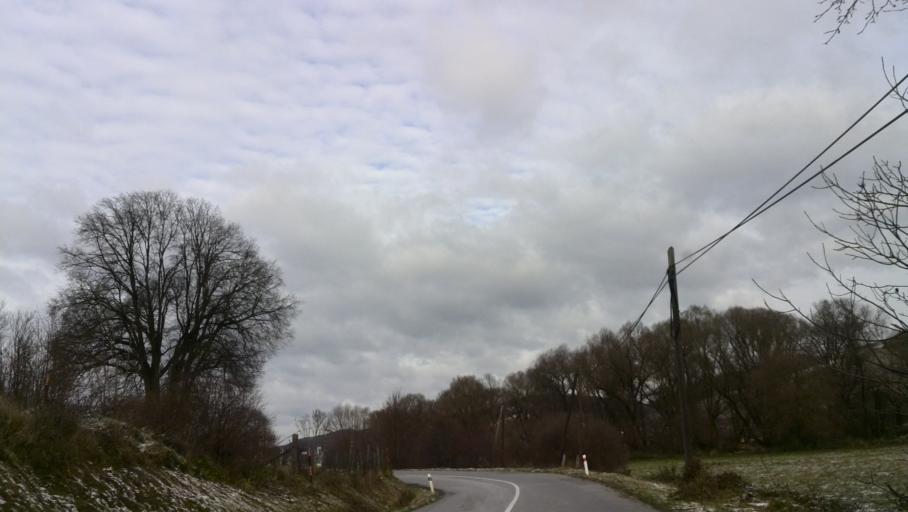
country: SK
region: Presovsky
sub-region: Okres Presov
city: Presov
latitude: 48.9223
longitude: 21.1918
